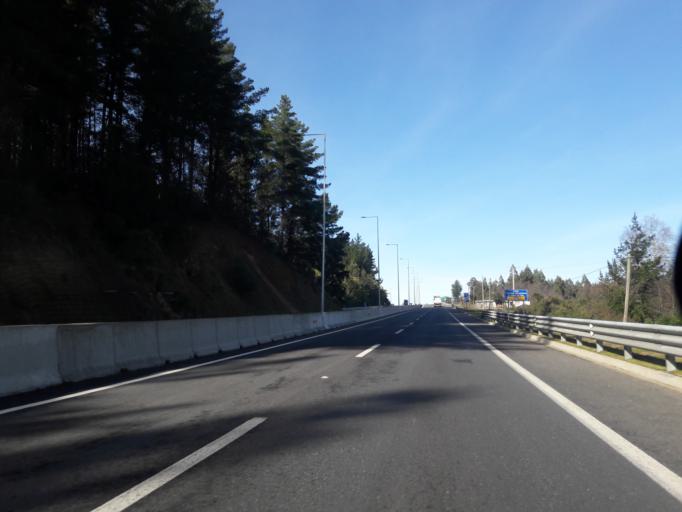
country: CL
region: Biobio
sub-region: Provincia de Concepcion
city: Chiguayante
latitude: -36.9292
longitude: -72.7670
